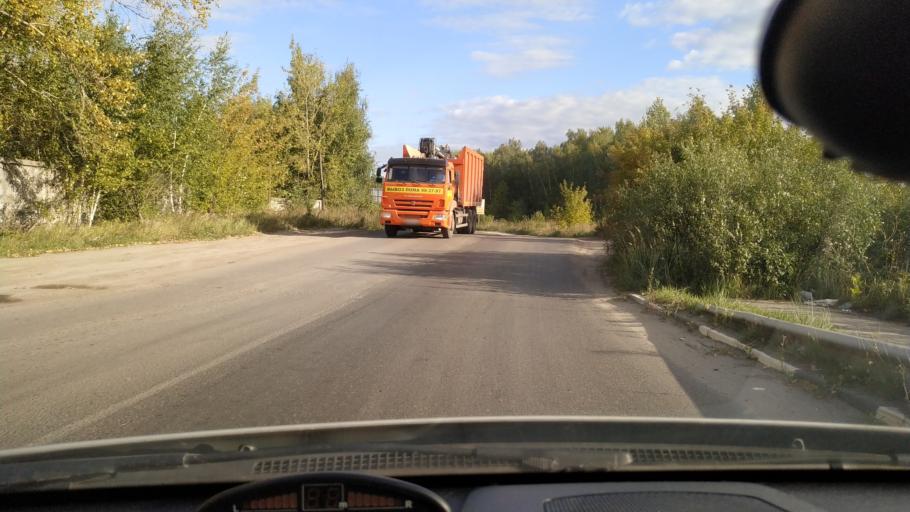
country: RU
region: Rjazan
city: Ryazan'
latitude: 54.5828
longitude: 39.8187
